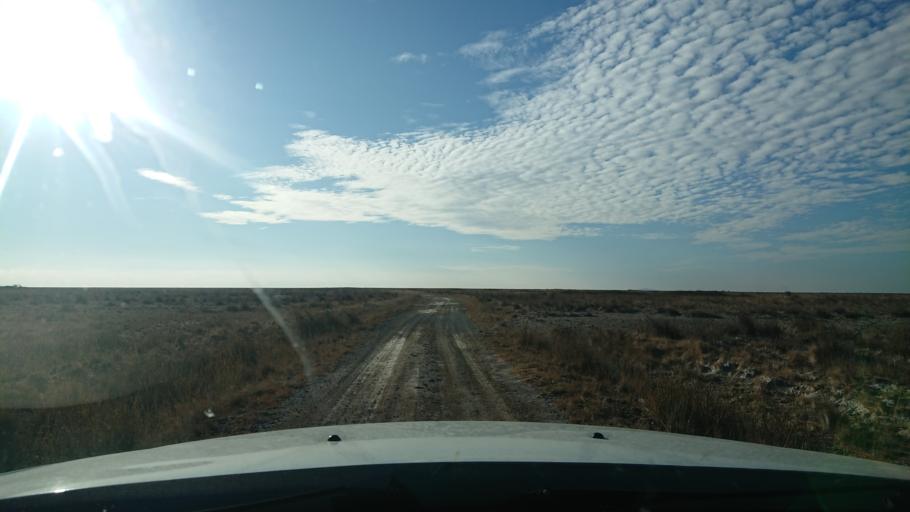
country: TR
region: Aksaray
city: Eskil
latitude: 38.5412
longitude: 33.3470
